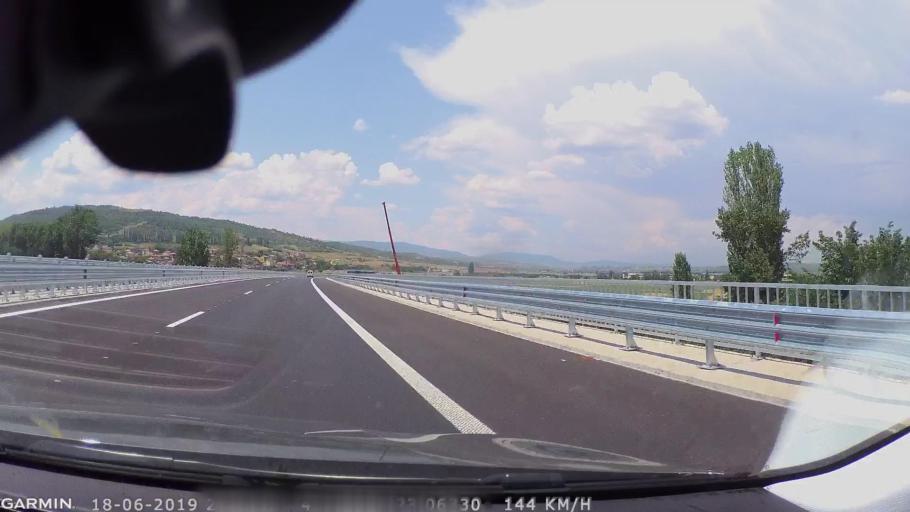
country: BG
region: Blagoevgrad
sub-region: Obshtina Blagoevgrad
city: Blagoevgrad
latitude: 41.9752
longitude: 23.0741
